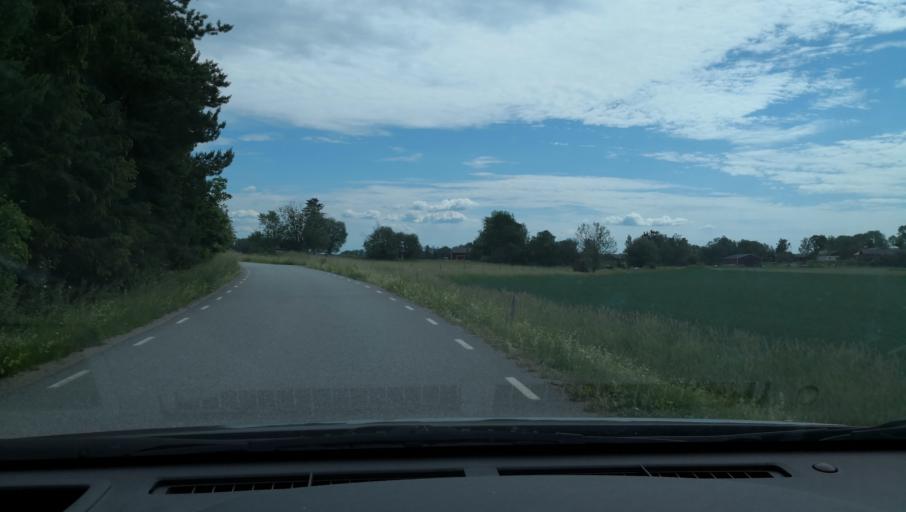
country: SE
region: Uppsala
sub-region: Enkopings Kommun
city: Orsundsbro
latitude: 59.6939
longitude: 17.4433
